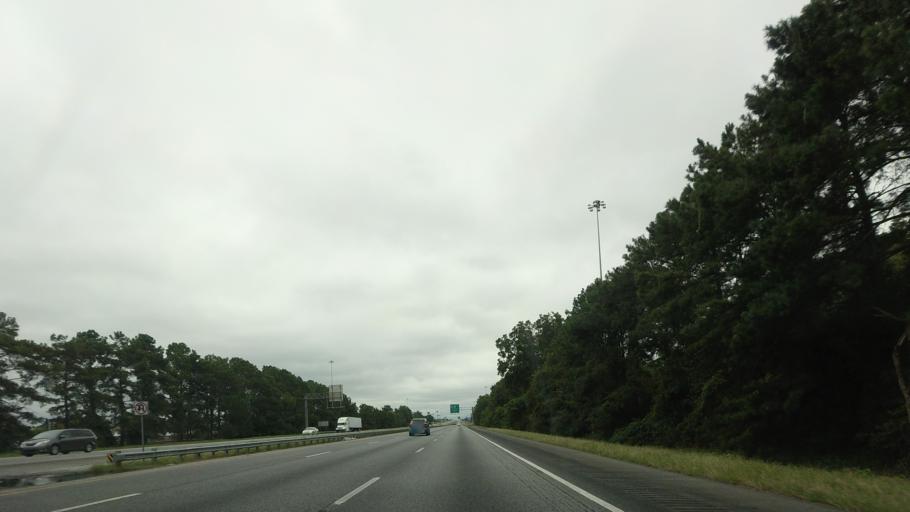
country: US
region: Georgia
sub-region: Lowndes County
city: Remerton
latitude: 30.8364
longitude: -83.3273
